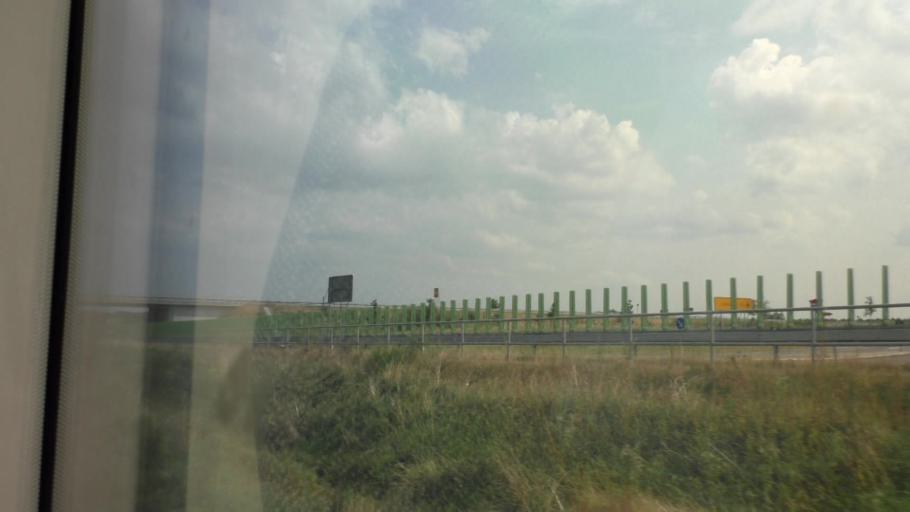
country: DE
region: Brandenburg
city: Beeskow
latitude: 52.1692
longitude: 14.2150
